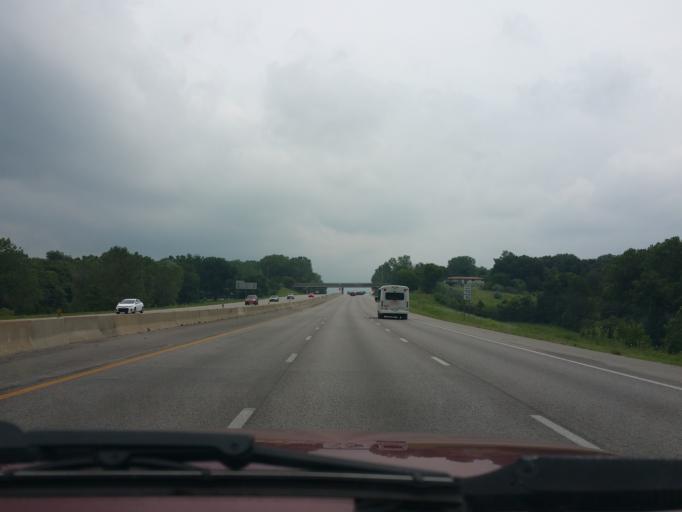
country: US
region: Kansas
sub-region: Johnson County
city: Shawnee
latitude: 39.1059
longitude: -94.7251
